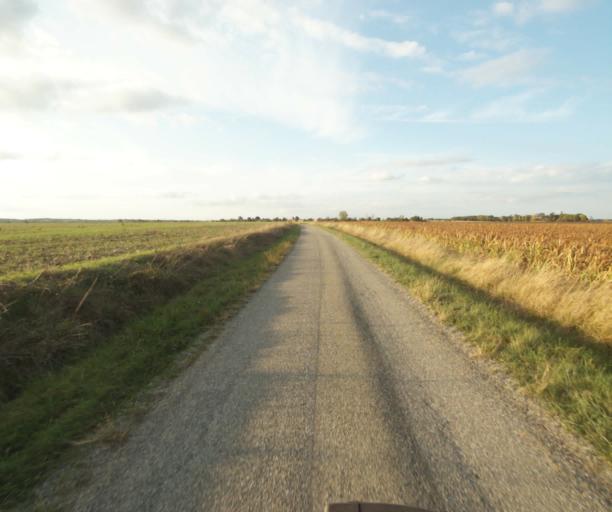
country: FR
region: Midi-Pyrenees
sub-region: Departement de la Haute-Garonne
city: Launac
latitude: 43.8152
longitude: 1.1626
